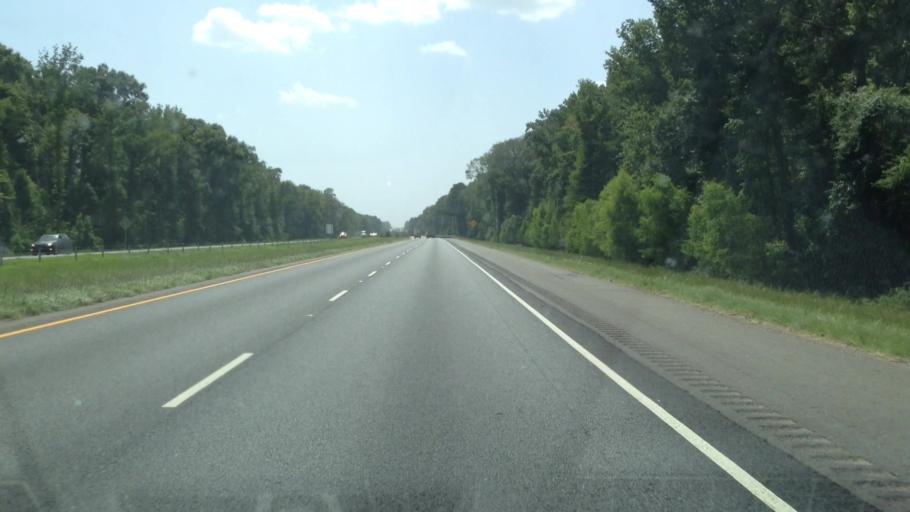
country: US
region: Louisiana
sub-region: Bienville Parish
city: Arcadia
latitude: 32.5636
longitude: -93.0857
